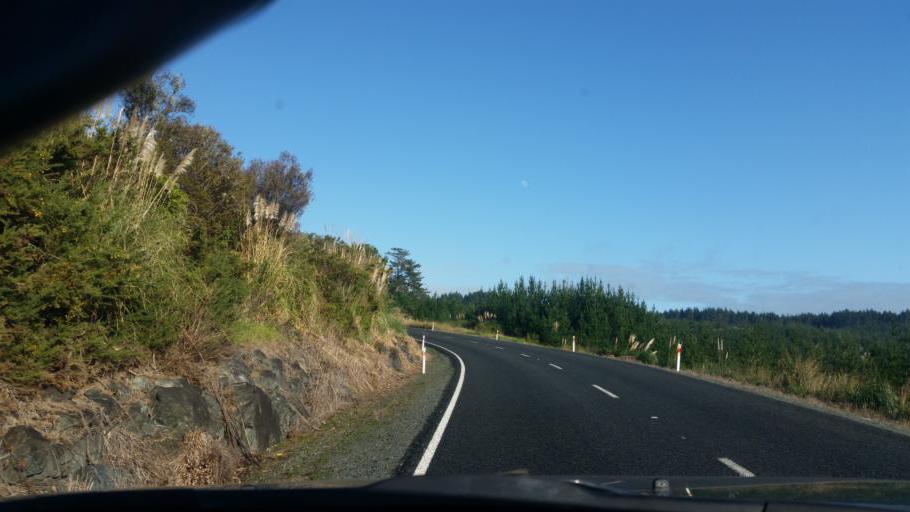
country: NZ
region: Auckland
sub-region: Auckland
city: Wellsford
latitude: -36.2215
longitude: 174.4602
